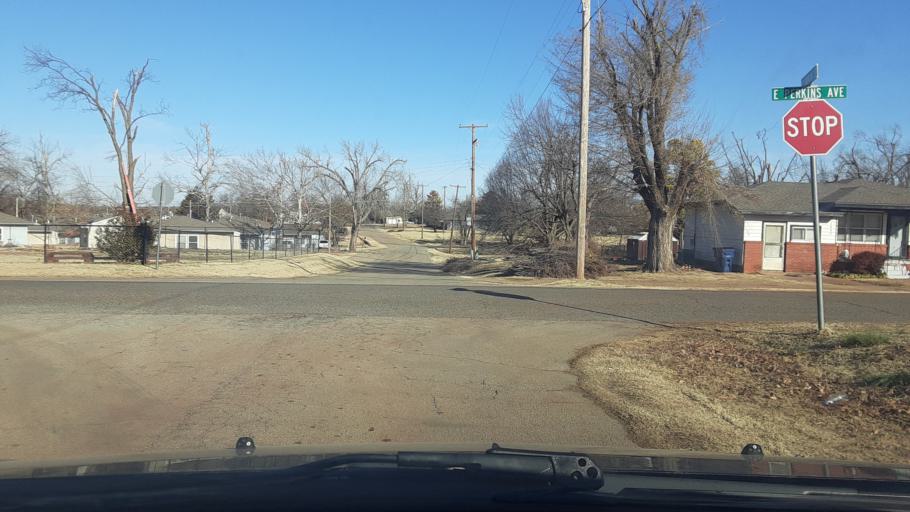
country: US
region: Oklahoma
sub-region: Logan County
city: Guthrie
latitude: 35.8738
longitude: -97.4039
